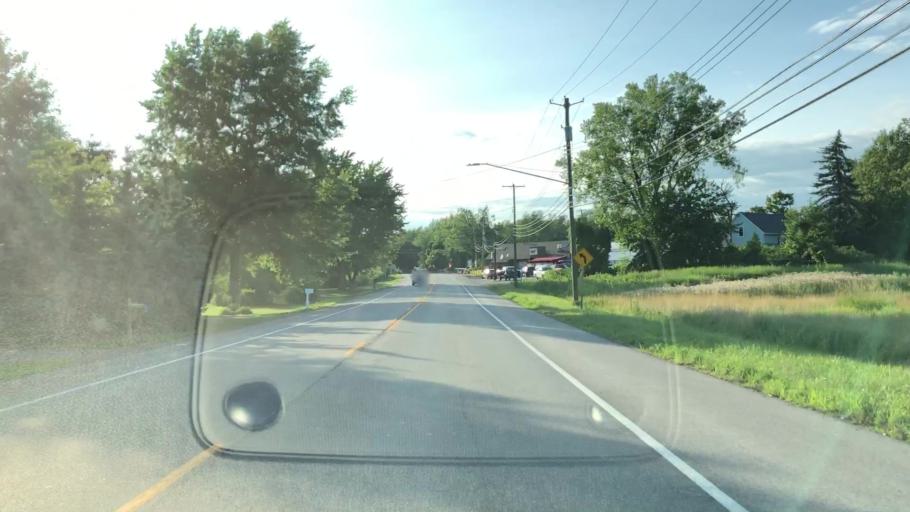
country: US
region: New York
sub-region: Erie County
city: West Seneca
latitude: 42.8669
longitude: -78.7743
